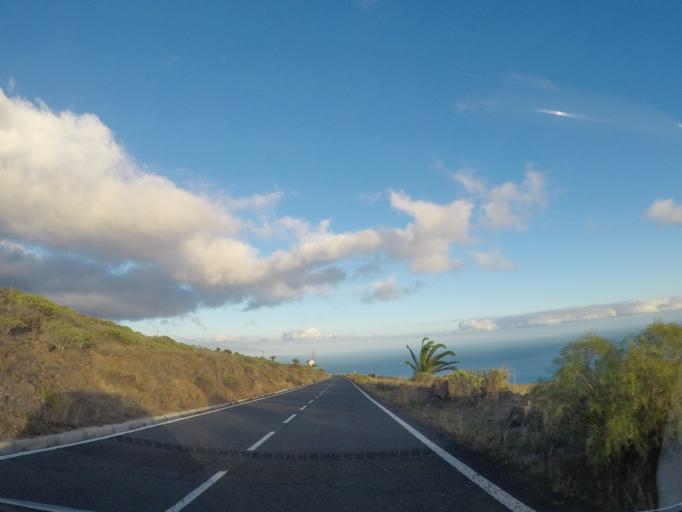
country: ES
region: Canary Islands
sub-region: Provincia de Santa Cruz de Tenerife
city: Alajero
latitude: 28.0452
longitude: -17.2309
